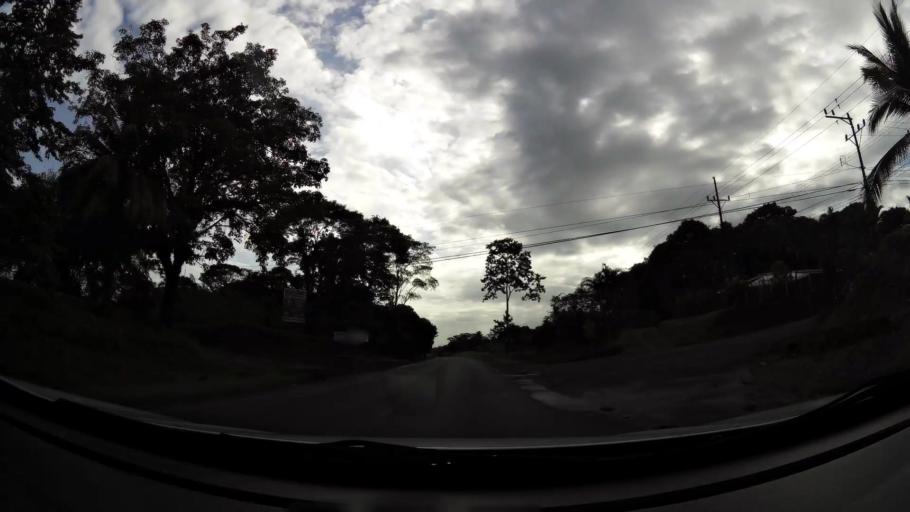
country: CR
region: Limon
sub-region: Canton de Guacimo
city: Guacimo
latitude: 10.2006
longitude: -83.6737
